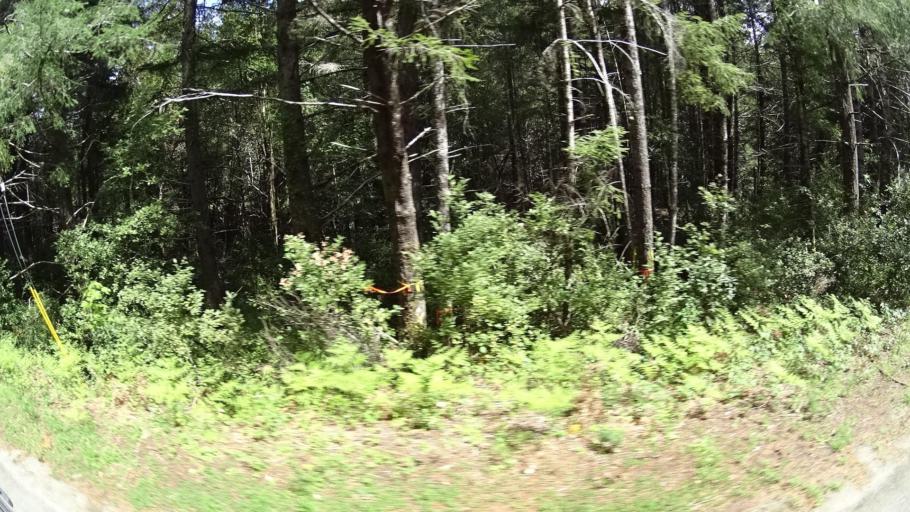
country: US
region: California
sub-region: Humboldt County
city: Redway
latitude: 40.0744
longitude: -123.9573
